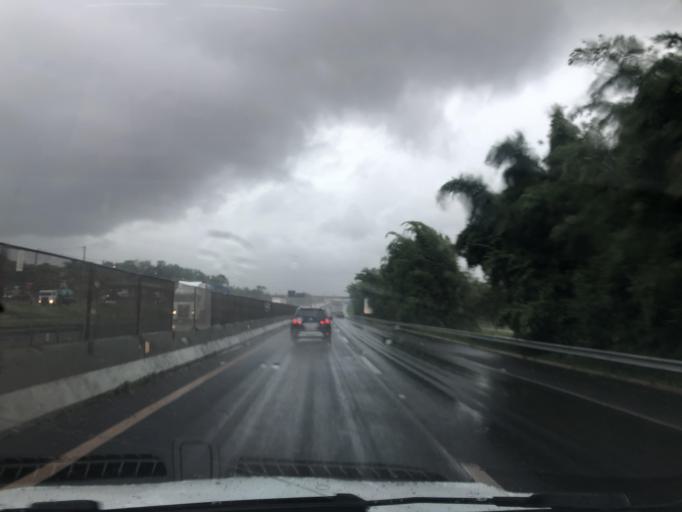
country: BR
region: Sao Paulo
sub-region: Ribeirao Preto
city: Ribeirao Preto
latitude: -21.1580
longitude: -47.7565
